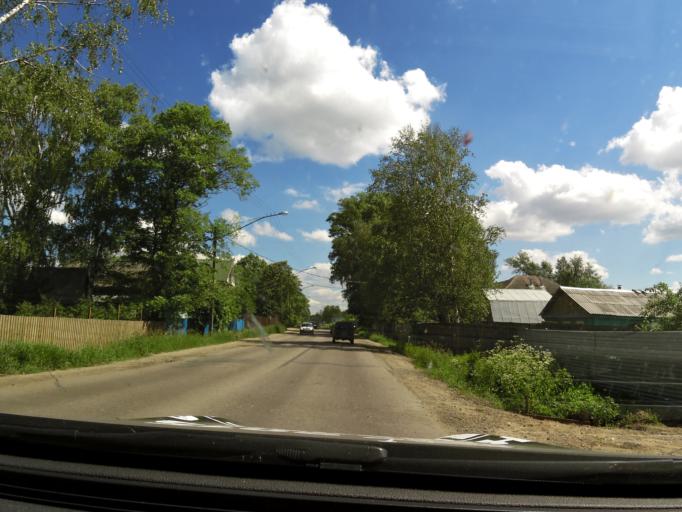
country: RU
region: Vologda
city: Vologda
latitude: 59.2385
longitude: 39.8040
